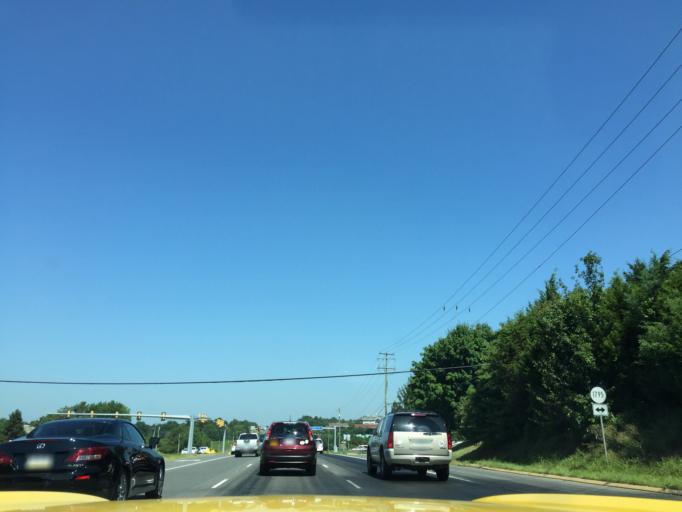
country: US
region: Virginia
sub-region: Loudoun County
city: Dulles Town Center
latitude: 39.0329
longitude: -77.4062
